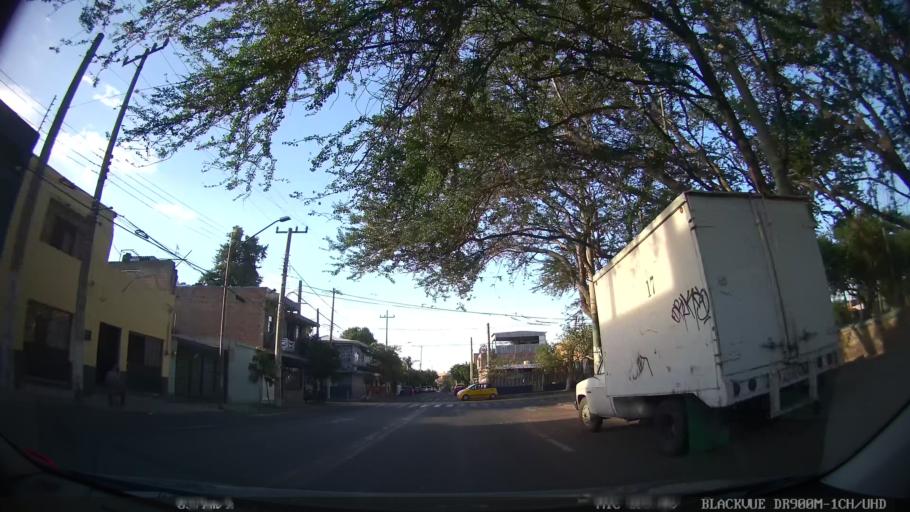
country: MX
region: Jalisco
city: Tlaquepaque
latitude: 20.7098
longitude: -103.3076
